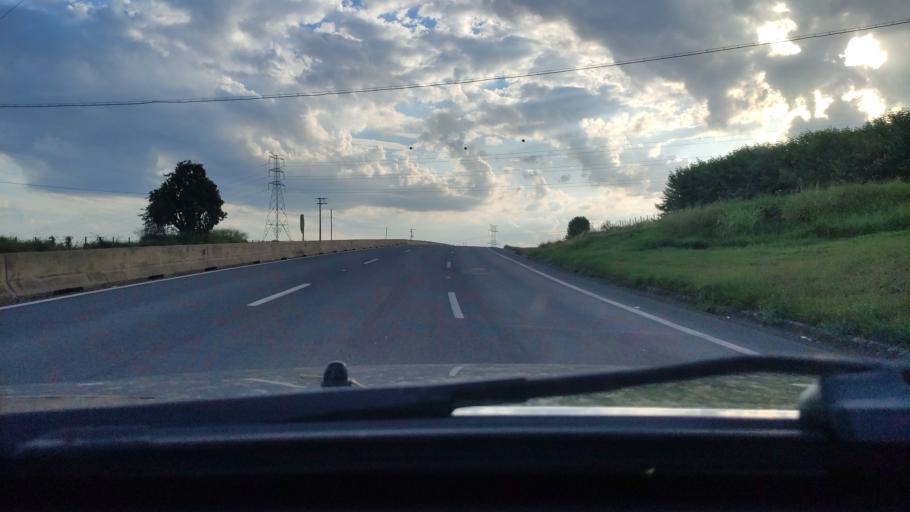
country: BR
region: Sao Paulo
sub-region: Mogi-Mirim
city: Mogi Mirim
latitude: -22.4498
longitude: -47.0611
